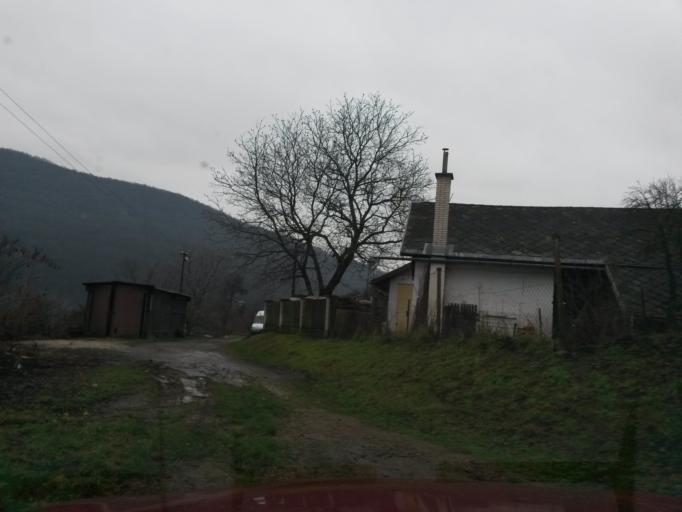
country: SK
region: Kosicky
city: Dobsina
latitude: 48.7419
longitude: 20.4141
